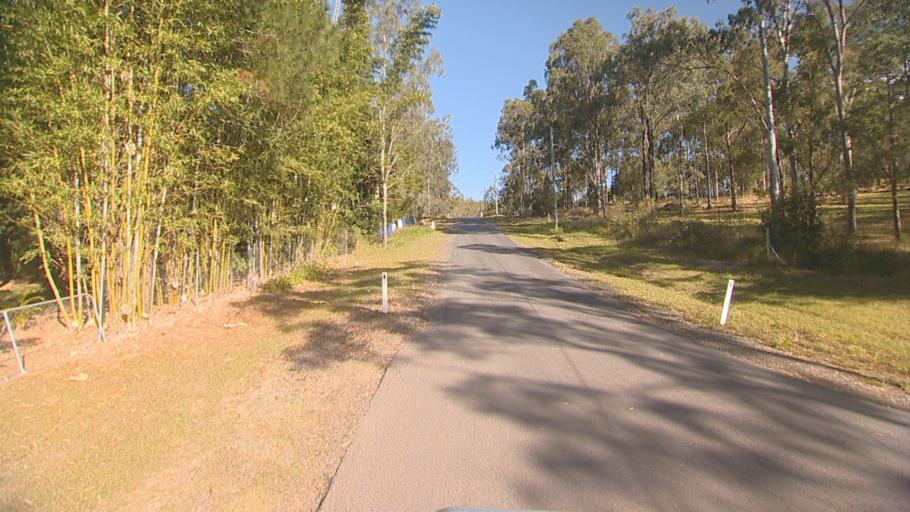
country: AU
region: Queensland
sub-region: Logan
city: Chambers Flat
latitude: -27.8210
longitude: 153.0799
